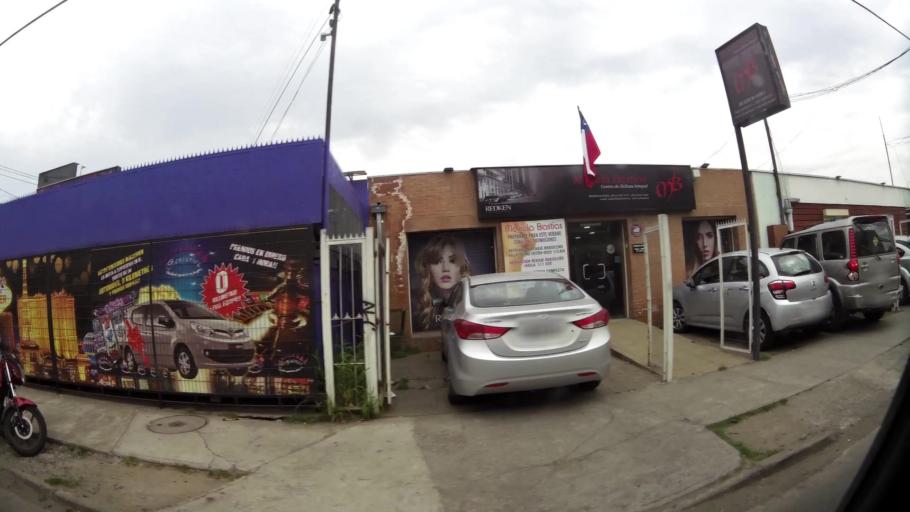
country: CL
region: Santiago Metropolitan
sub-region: Provincia de Santiago
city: Lo Prado
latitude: -33.5092
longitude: -70.7602
